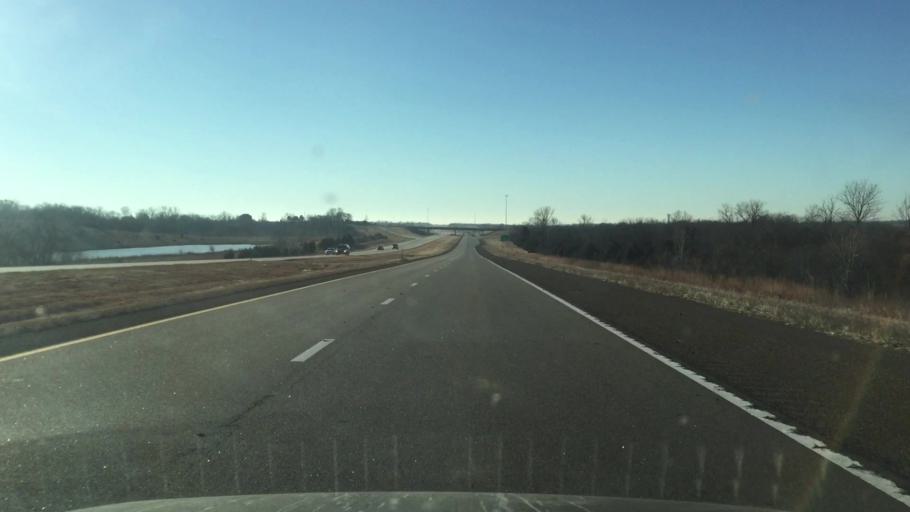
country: US
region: Kansas
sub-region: Miami County
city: Paola
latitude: 38.6298
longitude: -94.8361
